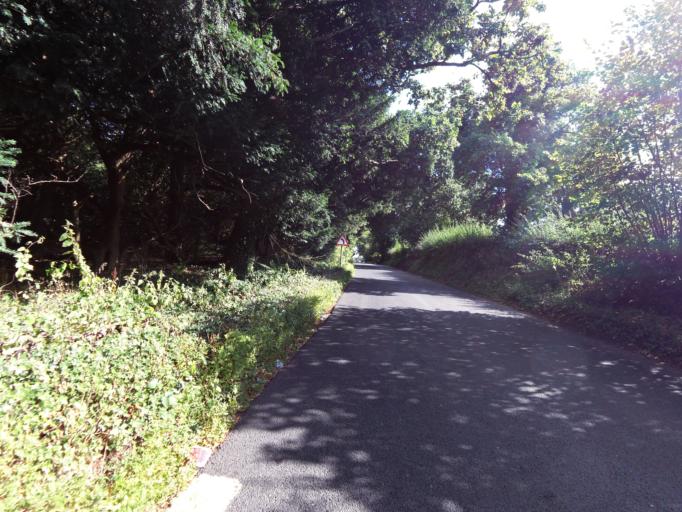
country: GB
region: England
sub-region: Greater London
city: High Barnet
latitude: 51.6718
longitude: -0.2376
